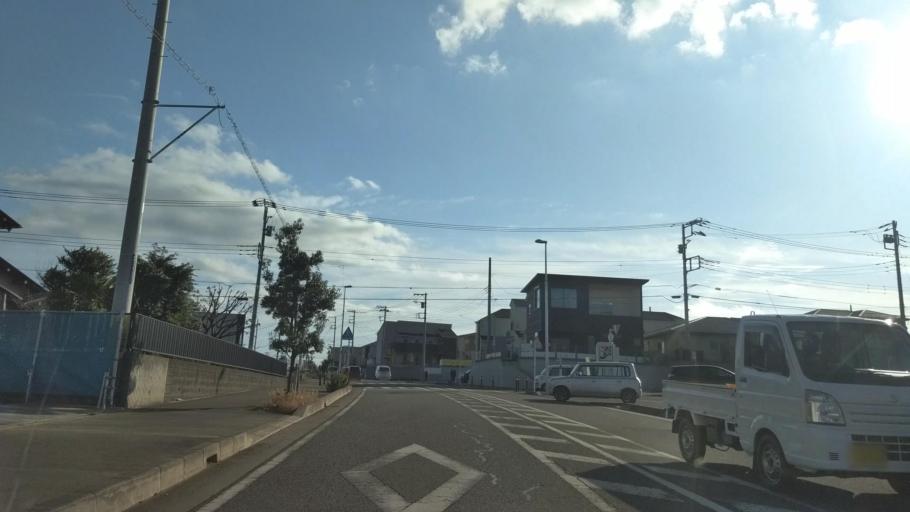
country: JP
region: Kanagawa
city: Isehara
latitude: 35.3702
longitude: 139.2837
